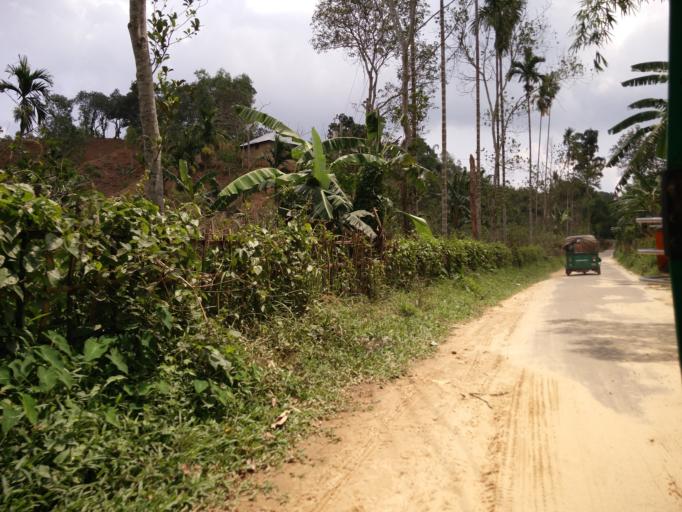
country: IN
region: Tripura
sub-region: Dhalai
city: Kamalpur
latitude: 24.3036
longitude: 91.7848
